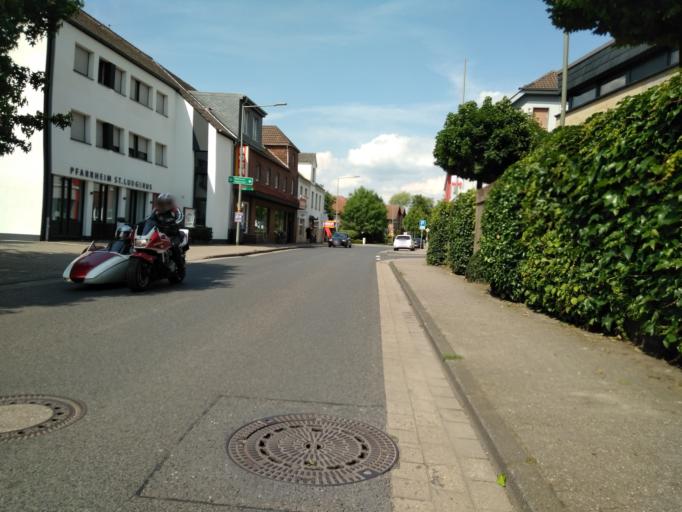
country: DE
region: North Rhine-Westphalia
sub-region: Regierungsbezirk Dusseldorf
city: Schermbeck
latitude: 51.6947
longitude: 6.8738
